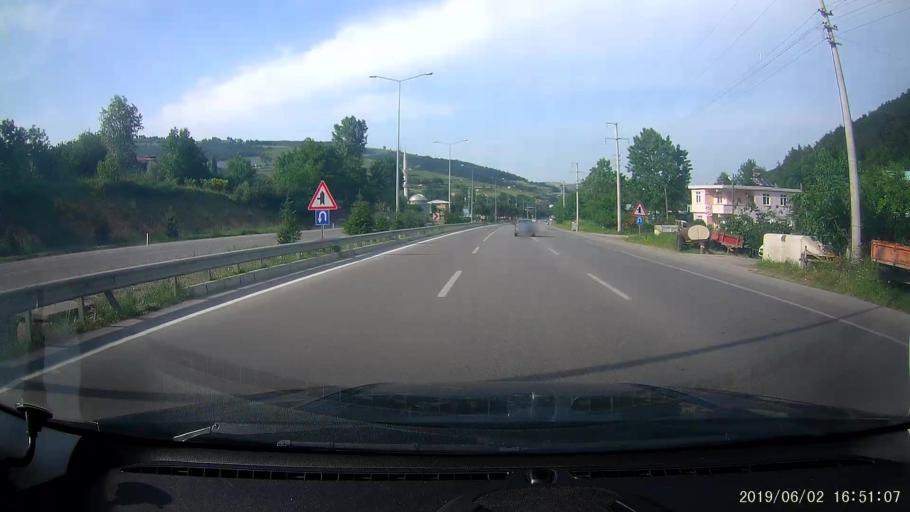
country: TR
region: Samsun
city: Taflan
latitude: 41.2688
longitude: 36.1783
